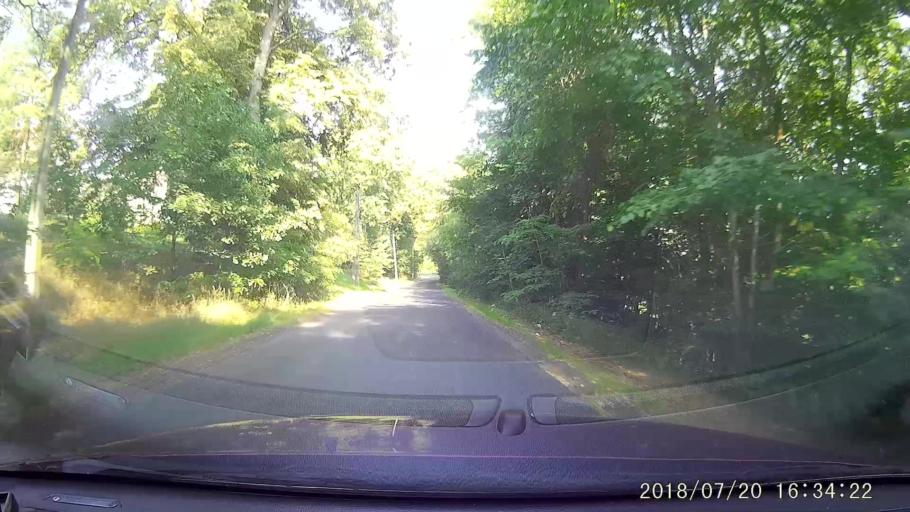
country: PL
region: Lower Silesian Voivodeship
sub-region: Powiat zgorzelecki
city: Sulikow
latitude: 51.0832
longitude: 15.0979
